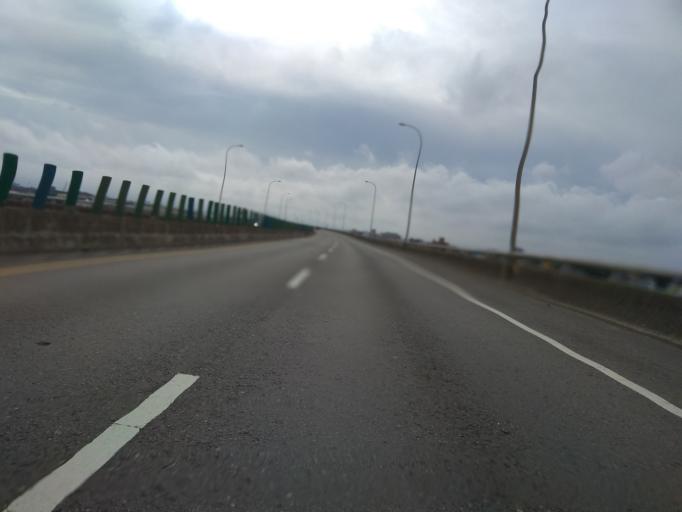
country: TW
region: Taiwan
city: Daxi
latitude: 24.9066
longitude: 121.2307
